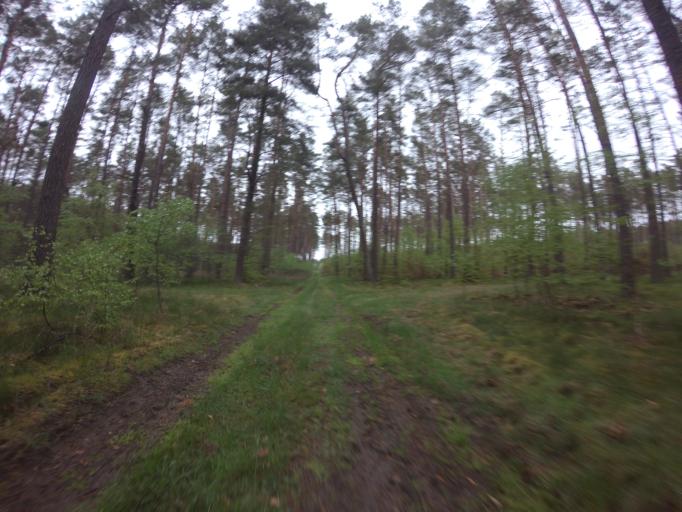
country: PL
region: West Pomeranian Voivodeship
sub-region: Powiat drawski
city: Kalisz Pomorski
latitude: 53.2187
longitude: 16.0103
